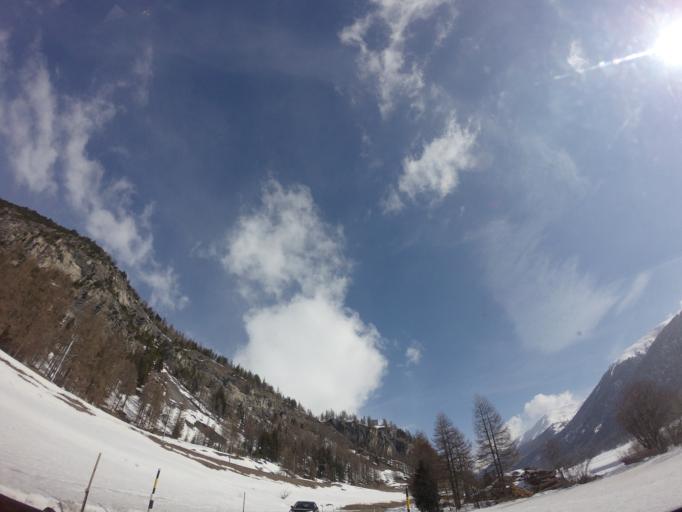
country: CH
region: Grisons
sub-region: Maloja District
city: Ponte
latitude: 46.5828
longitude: 9.9289
